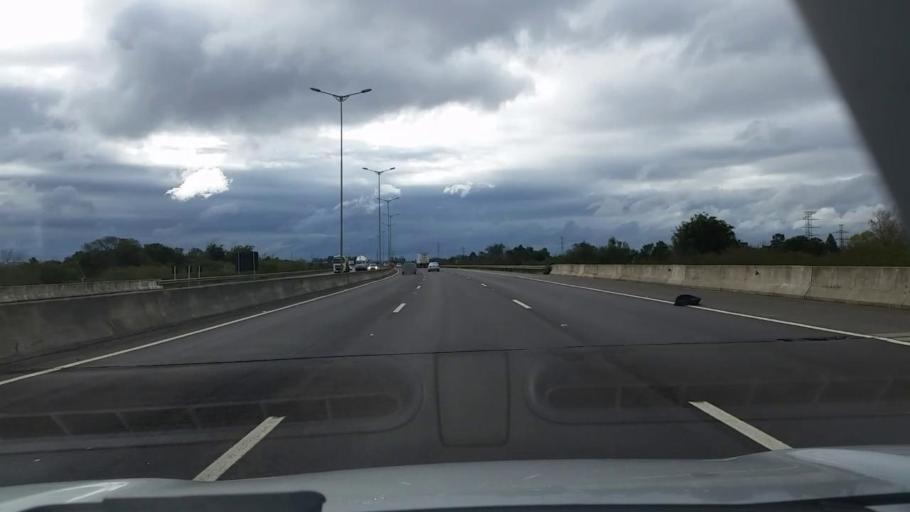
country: BR
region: Rio Grande do Sul
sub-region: Canoas
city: Canoas
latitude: -29.9413
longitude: -51.2053
